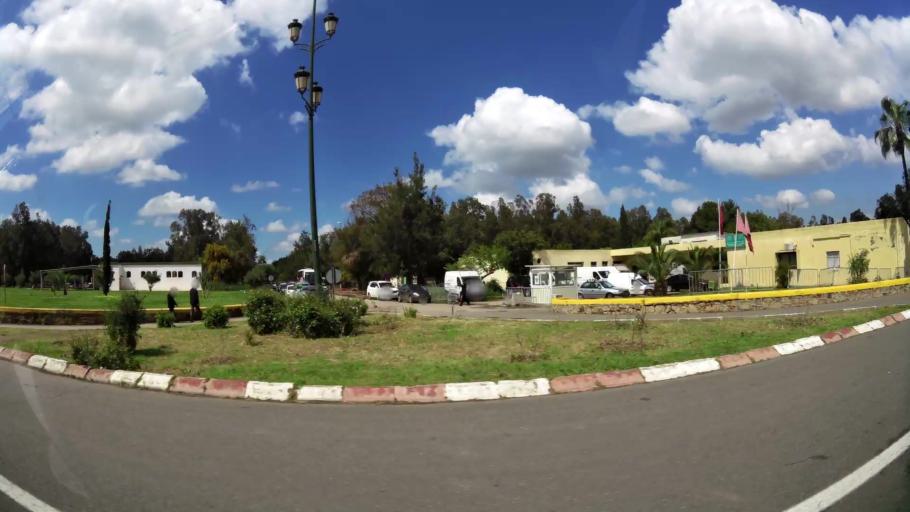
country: MA
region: Chaouia-Ouardigha
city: Nouaseur
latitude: 33.3766
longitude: -7.5779
